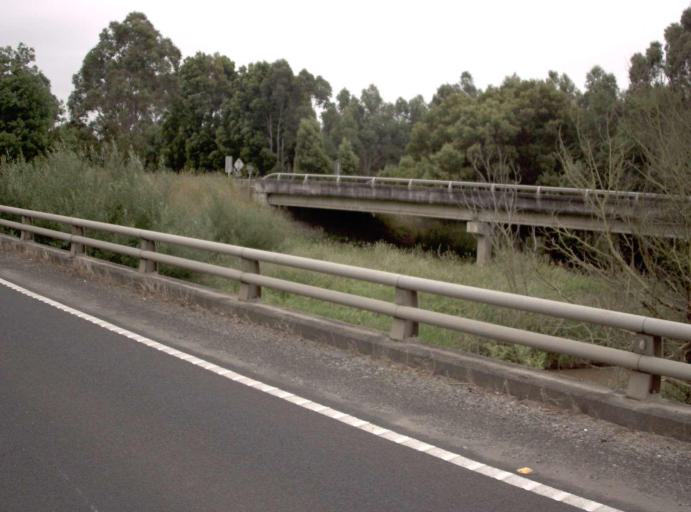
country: AU
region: Victoria
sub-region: Latrobe
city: Morwell
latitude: -38.2293
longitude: 146.3626
